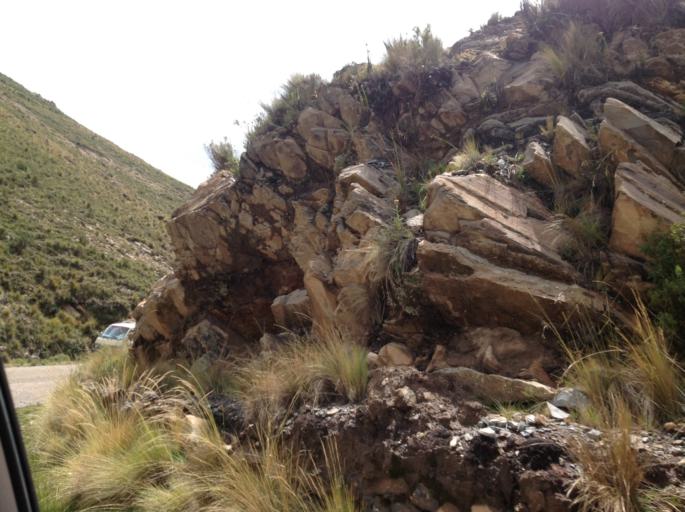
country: BO
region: La Paz
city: Yumani
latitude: -15.7734
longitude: -69.0058
